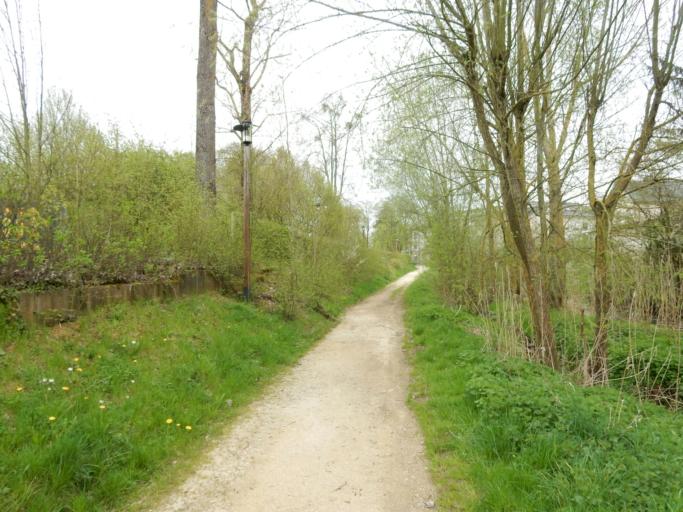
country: LU
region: Luxembourg
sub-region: Canton d'Esch-sur-Alzette
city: Petange
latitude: 49.5599
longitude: 5.8741
